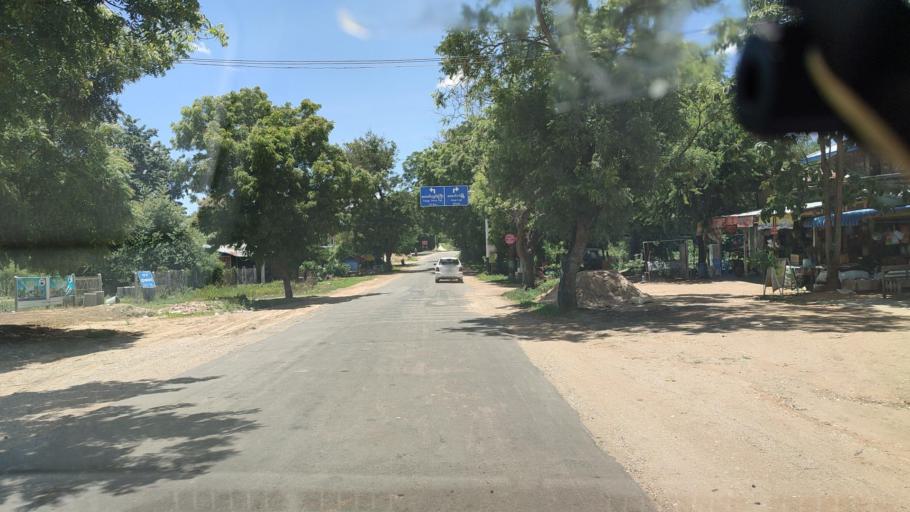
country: MM
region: Magway
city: Taungdwingyi
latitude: 19.7094
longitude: 95.3842
